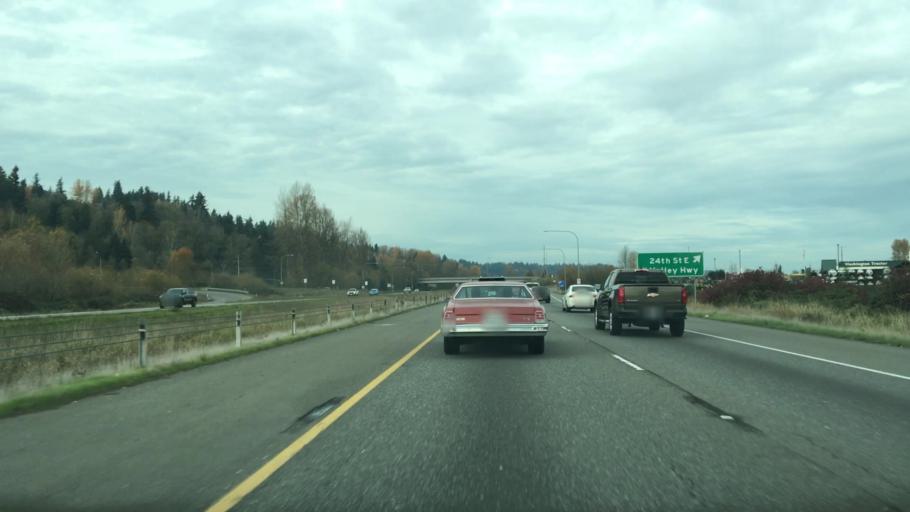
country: US
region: Washington
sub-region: Pierce County
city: Sumner
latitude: 47.2308
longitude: -122.2495
